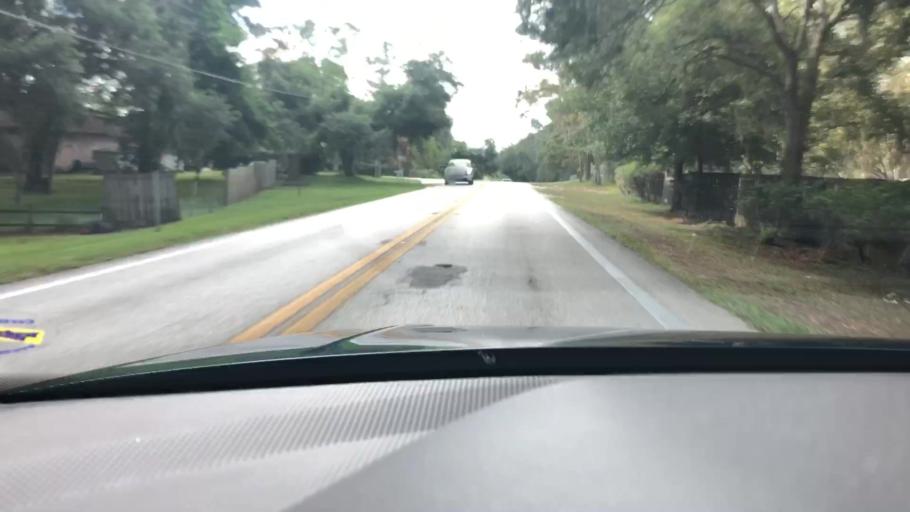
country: US
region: Florida
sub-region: Polk County
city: Gibsonia
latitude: 28.1477
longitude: -81.9349
